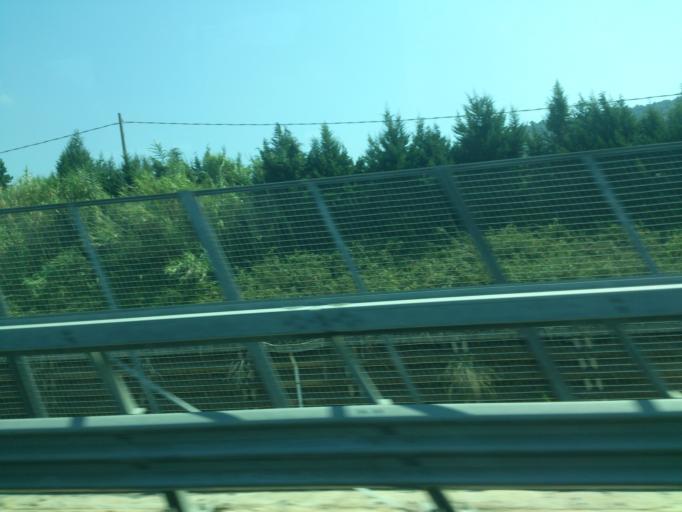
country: IT
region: Calabria
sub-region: Provincia di Catanzaro
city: Acconia
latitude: 38.8048
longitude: 16.2311
